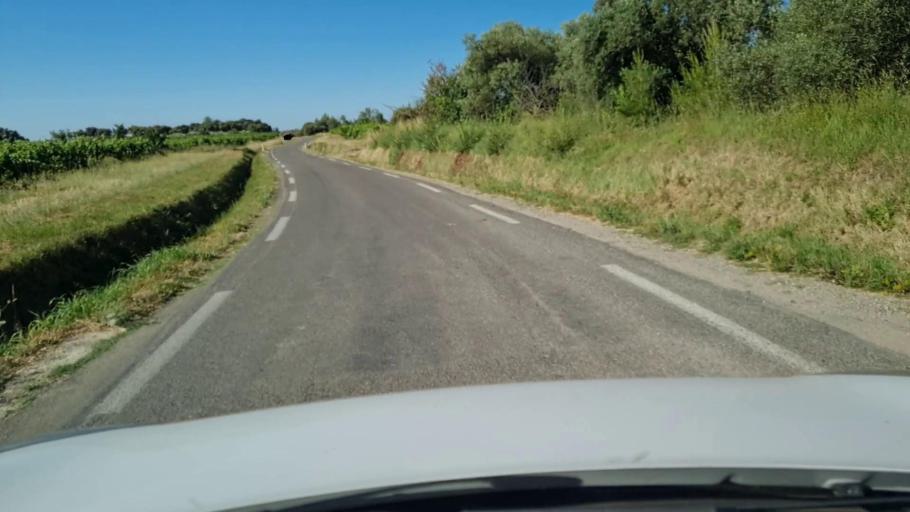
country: FR
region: Languedoc-Roussillon
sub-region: Departement du Gard
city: Sommieres
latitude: 43.8016
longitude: 4.0382
